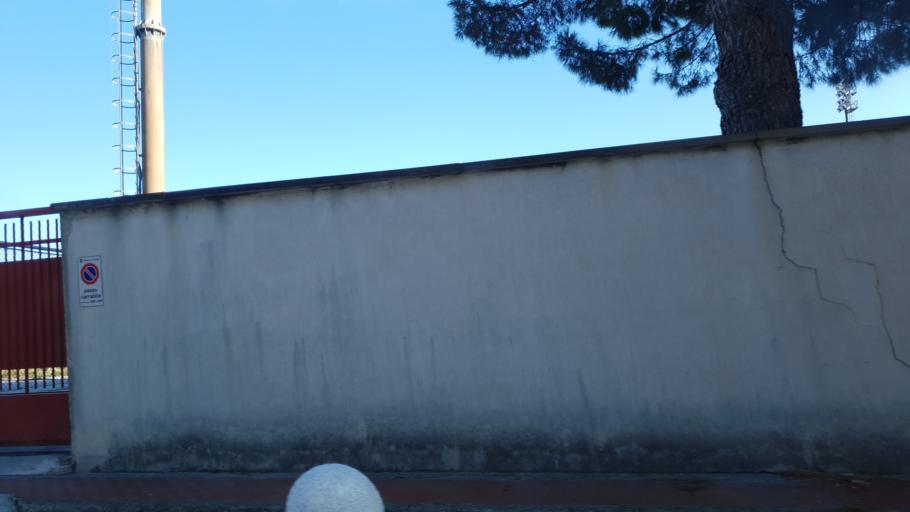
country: IT
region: Liguria
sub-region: Provincia di Savona
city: Valleggia
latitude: 44.2771
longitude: 8.4343
